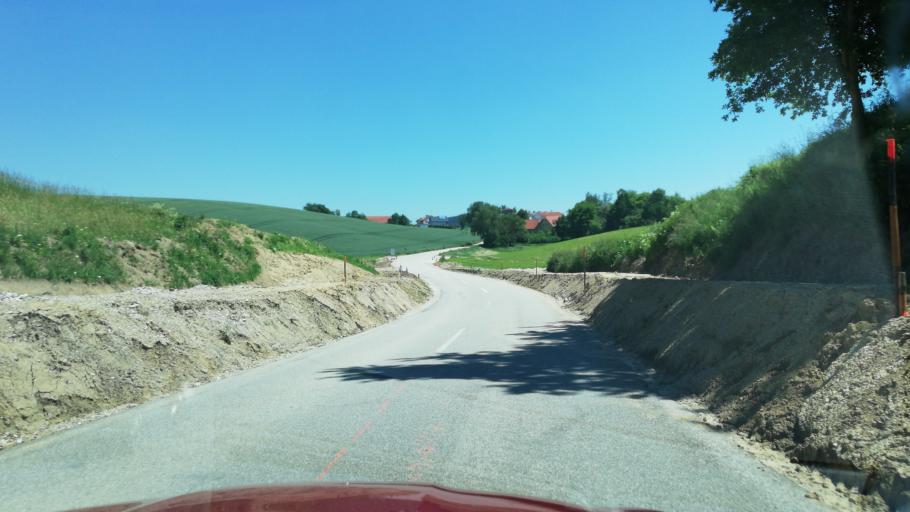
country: AT
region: Upper Austria
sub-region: Wels-Land
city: Bachmanning
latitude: 48.1288
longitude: 13.7748
